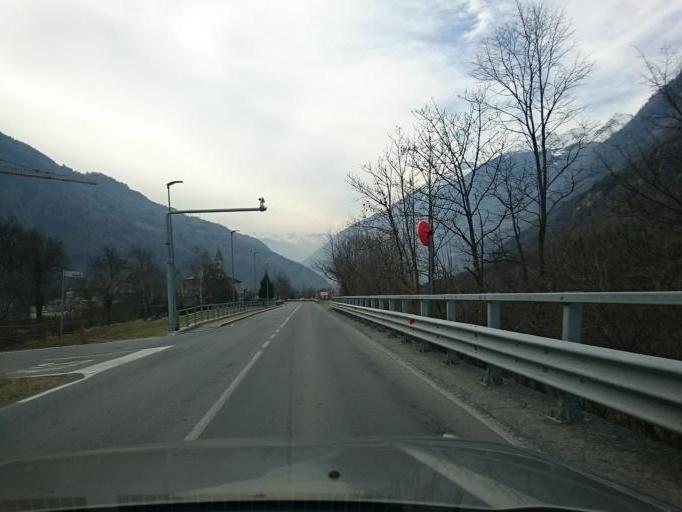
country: IT
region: Lombardy
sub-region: Provincia di Sondrio
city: Sondalo
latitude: 46.3159
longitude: 10.3022
